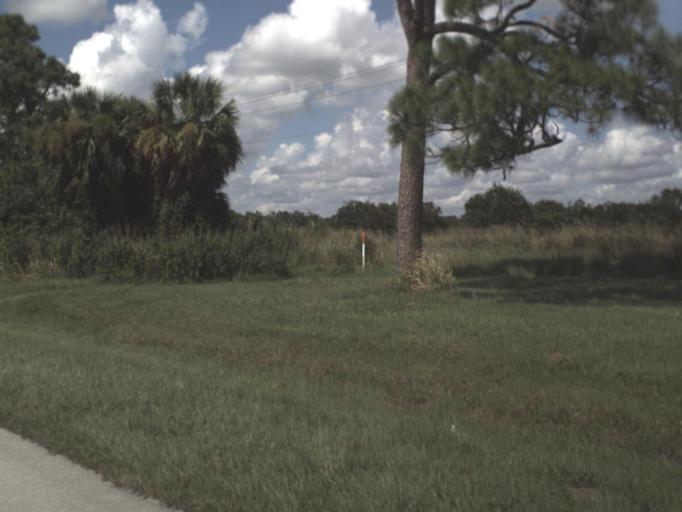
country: US
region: Florida
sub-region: Collier County
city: Immokalee
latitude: 26.5032
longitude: -81.5039
